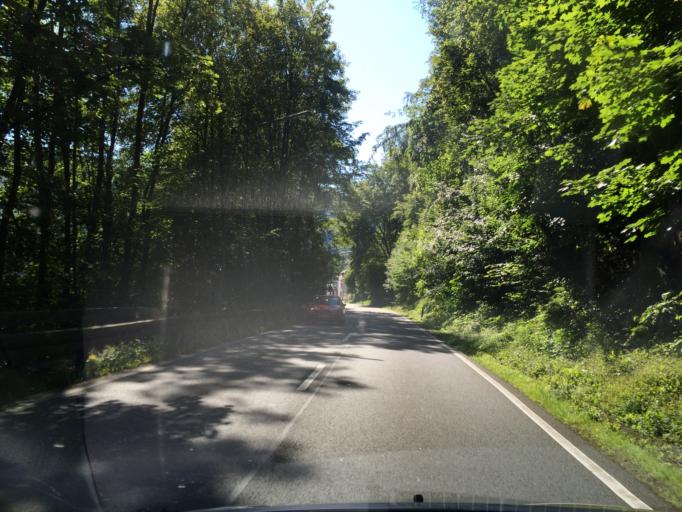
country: DE
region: North Rhine-Westphalia
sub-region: Regierungsbezirk Arnsberg
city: Nachrodt-Wiblingwerde
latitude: 51.3355
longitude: 7.6450
